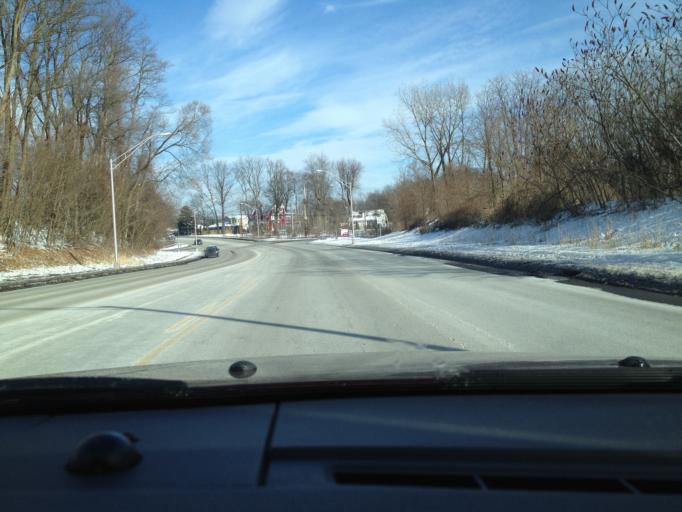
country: US
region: New York
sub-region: Albany County
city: West Albany
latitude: 42.6863
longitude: -73.7811
